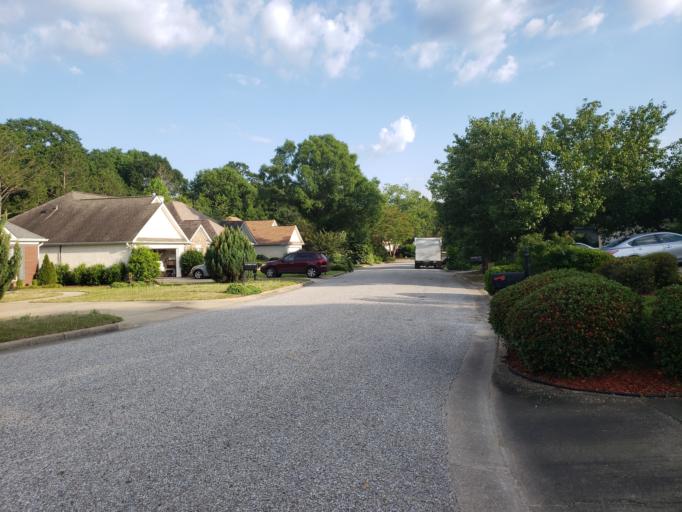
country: US
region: Alabama
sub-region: Lee County
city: Auburn
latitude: 32.5863
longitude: -85.4574
